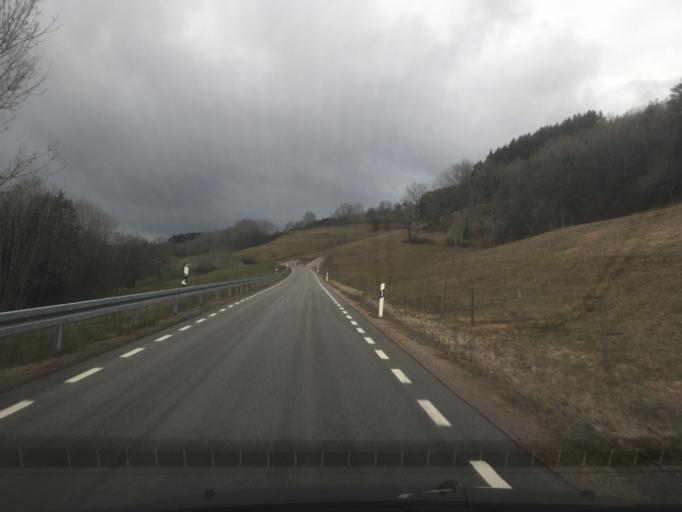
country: DE
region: Baden-Wuerttemberg
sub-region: Freiburg Region
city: Waldshut-Tiengen
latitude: 47.6583
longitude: 8.1841
